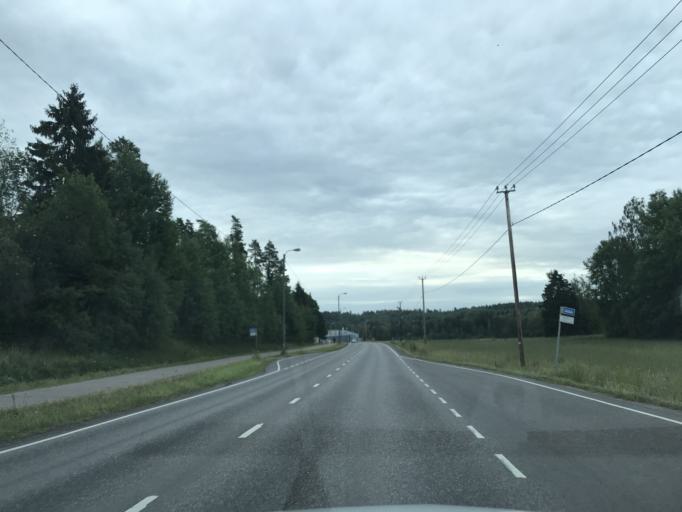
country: FI
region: Uusimaa
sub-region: Helsinki
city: Nurmijaervi
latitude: 60.3822
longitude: 24.7310
